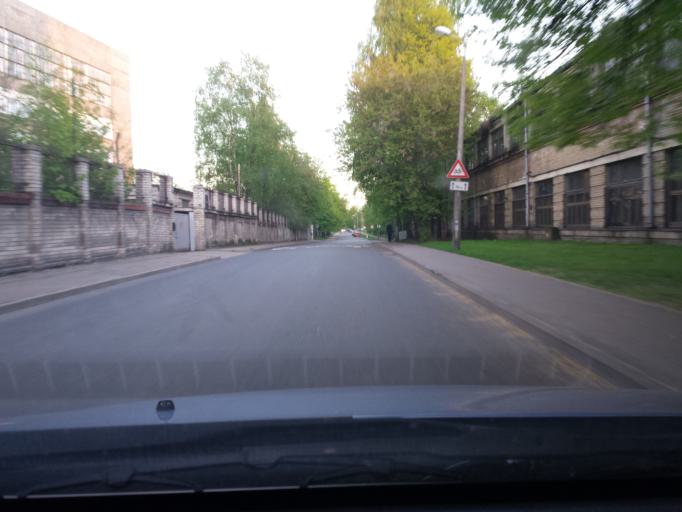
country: LV
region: Riga
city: Riga
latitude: 56.9918
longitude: 24.1315
